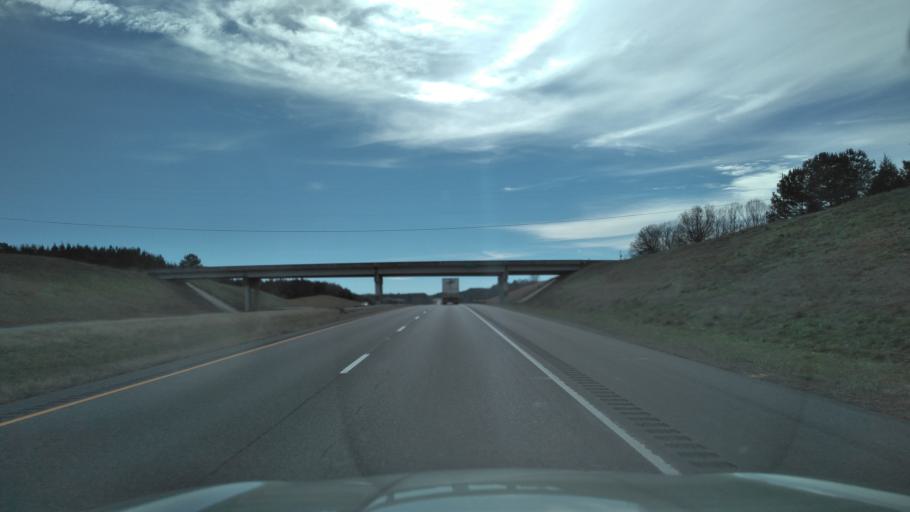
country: US
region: Alabama
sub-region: Marion County
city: Hamilton
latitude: 34.1487
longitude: -88.0594
